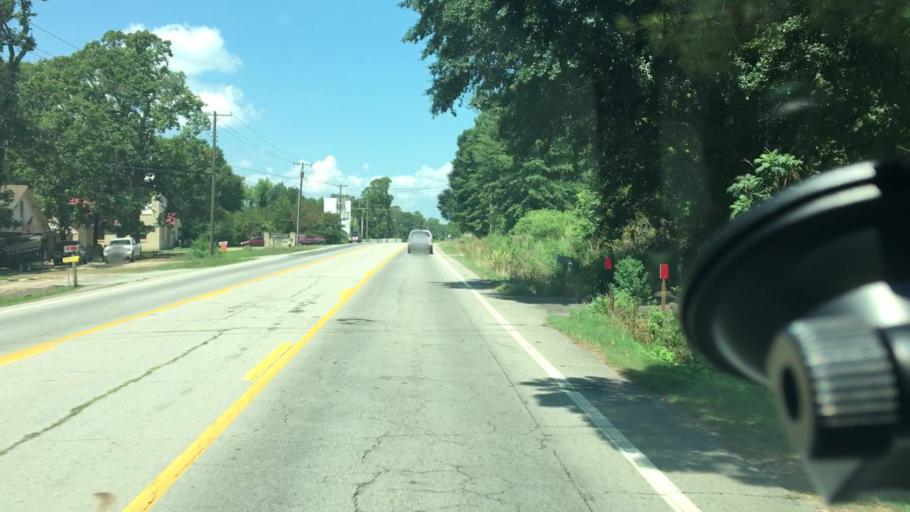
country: US
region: Arkansas
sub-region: Sebastian County
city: Lavaca
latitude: 35.2935
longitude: -94.1374
